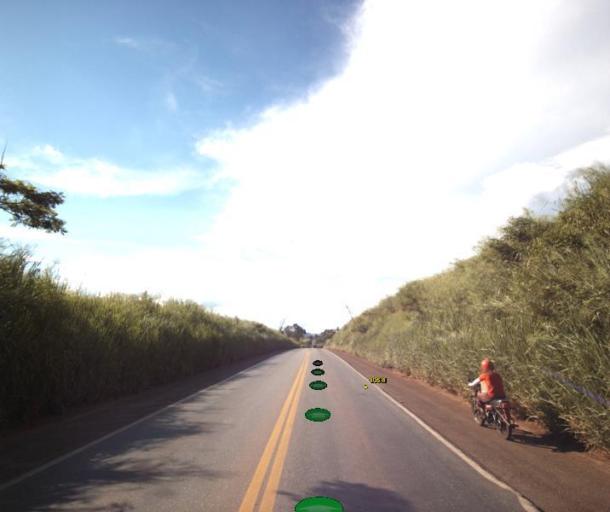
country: BR
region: Goias
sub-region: Rialma
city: Rialma
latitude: -15.3402
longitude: -49.5694
